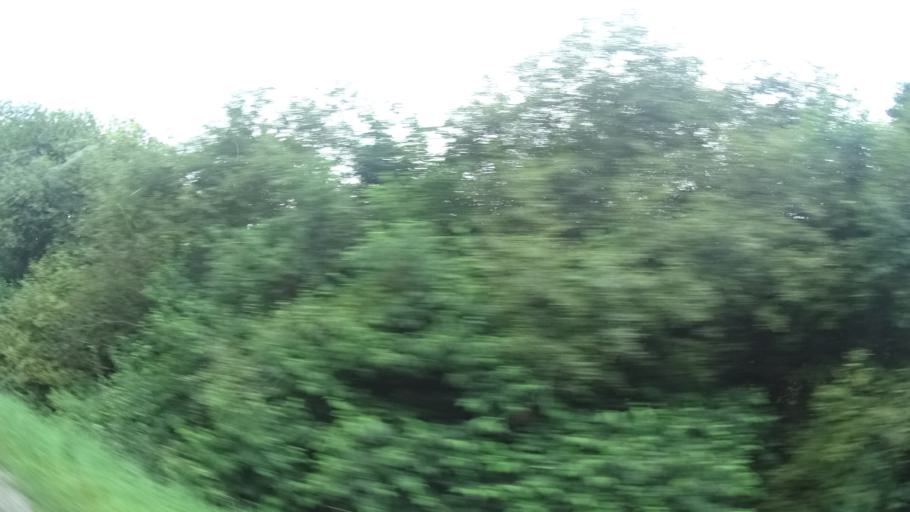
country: DE
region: Thuringia
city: Kaulsdorf
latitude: 50.6202
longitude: 11.4270
